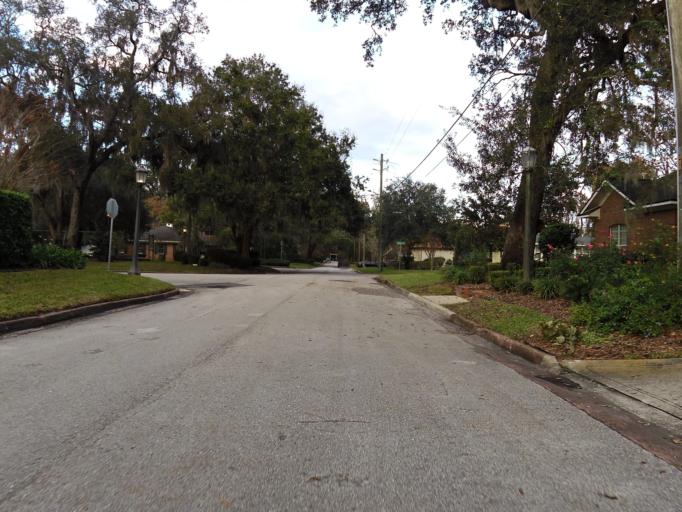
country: US
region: Florida
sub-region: Duval County
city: Jacksonville
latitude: 30.2826
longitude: -81.6585
